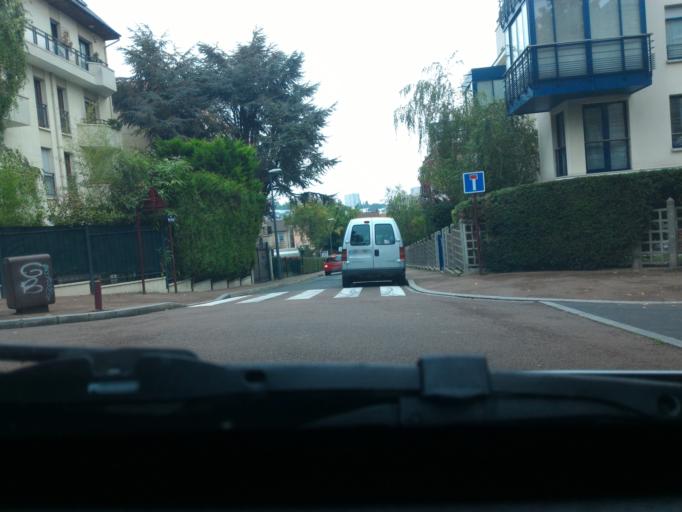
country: FR
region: Ile-de-France
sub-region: Departement des Hauts-de-Seine
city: Bourg-la-Reine
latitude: 48.7791
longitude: 2.3040
